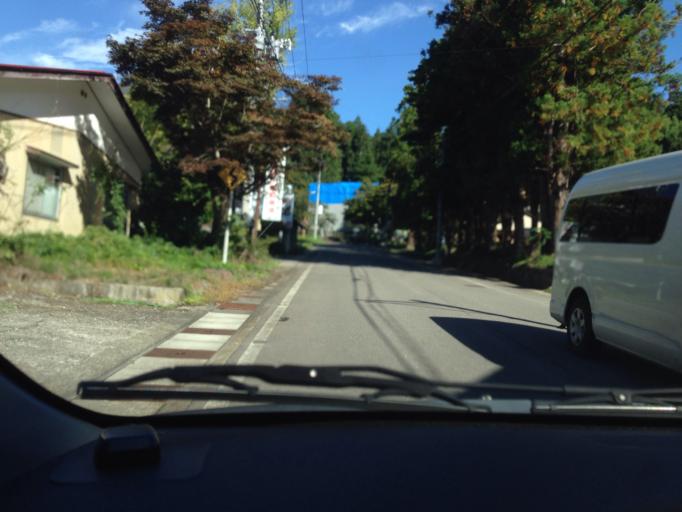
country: JP
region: Fukushima
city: Inawashiro
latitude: 37.5688
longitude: 140.1009
